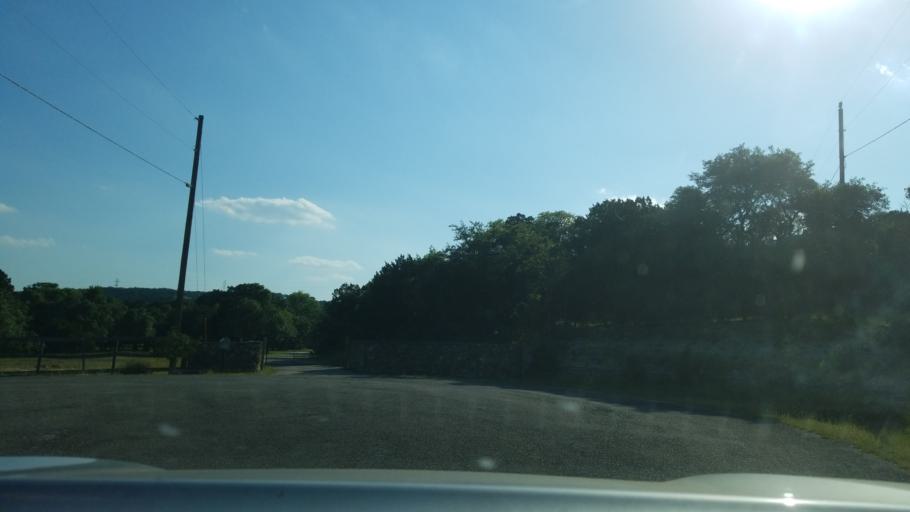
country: US
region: Texas
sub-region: Comal County
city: Bulverde
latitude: 29.7889
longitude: -98.4283
